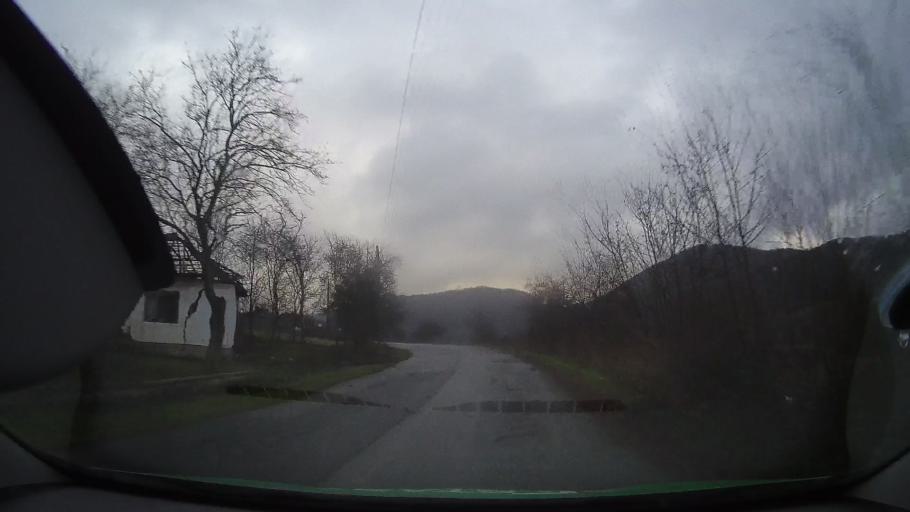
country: RO
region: Hunedoara
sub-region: Comuna Ribita
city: Ribita
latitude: 46.2286
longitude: 22.7331
